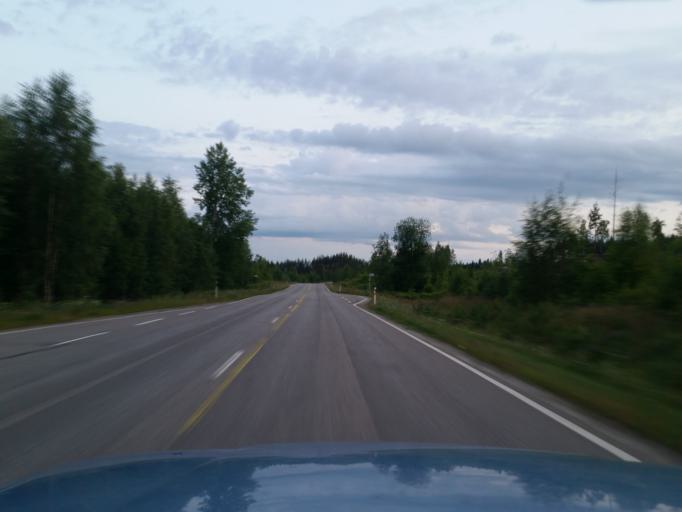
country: FI
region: Southern Savonia
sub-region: Savonlinna
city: Sulkava
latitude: 61.8144
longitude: 28.4324
